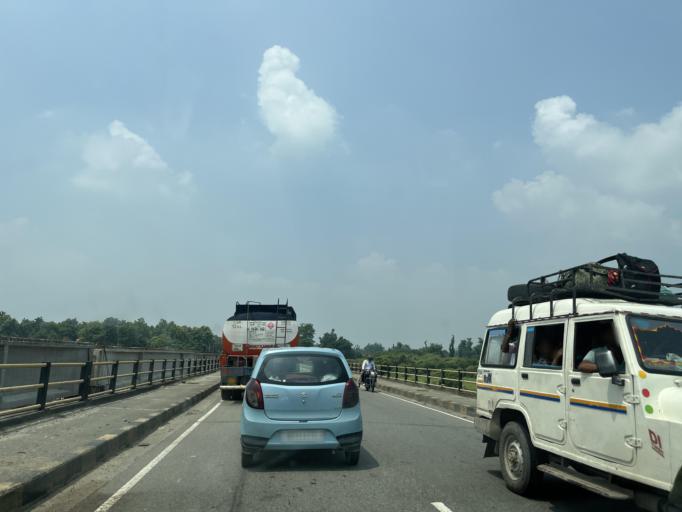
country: IN
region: Uttarakhand
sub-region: Haridwar
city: Haridwar
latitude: 29.8405
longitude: 78.1931
